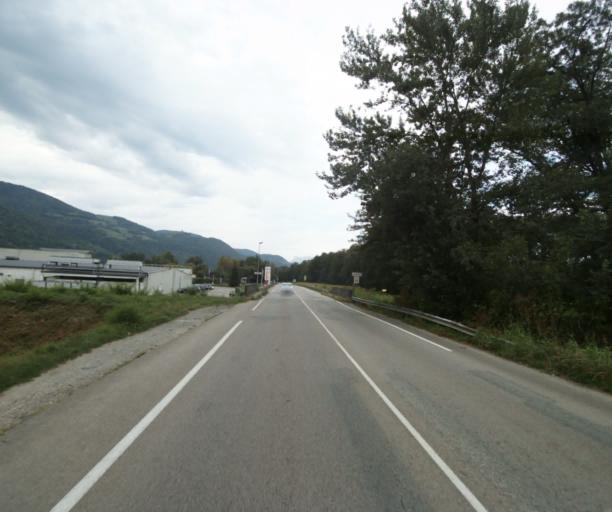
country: FR
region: Rhone-Alpes
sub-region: Departement de l'Isere
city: Domene
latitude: 45.2080
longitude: 5.8285
